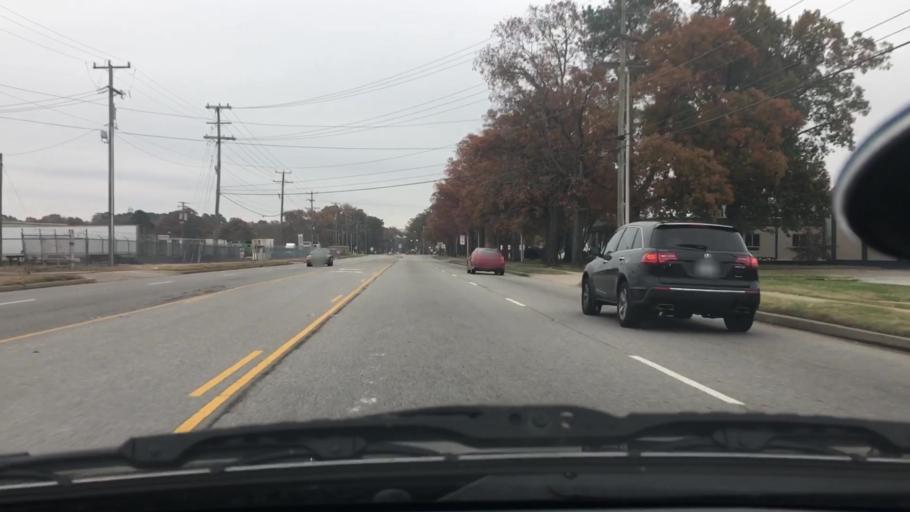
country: US
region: Virginia
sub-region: City of Norfolk
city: Norfolk
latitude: 36.8577
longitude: -76.2416
